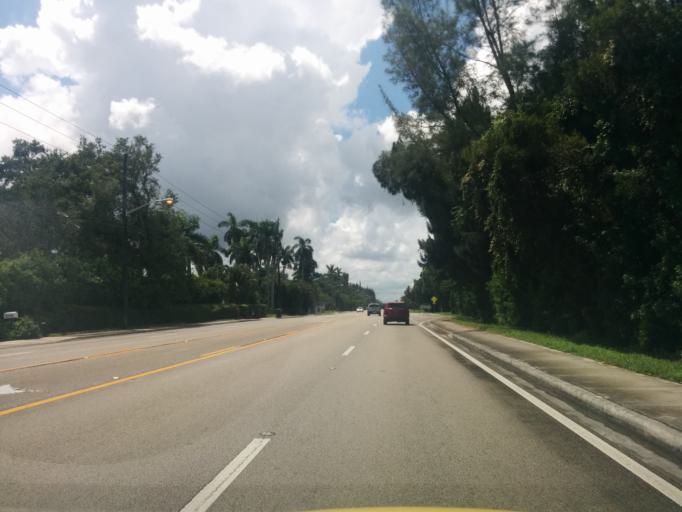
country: US
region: Florida
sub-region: Broward County
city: Davie
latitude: 26.0549
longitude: -80.2318
